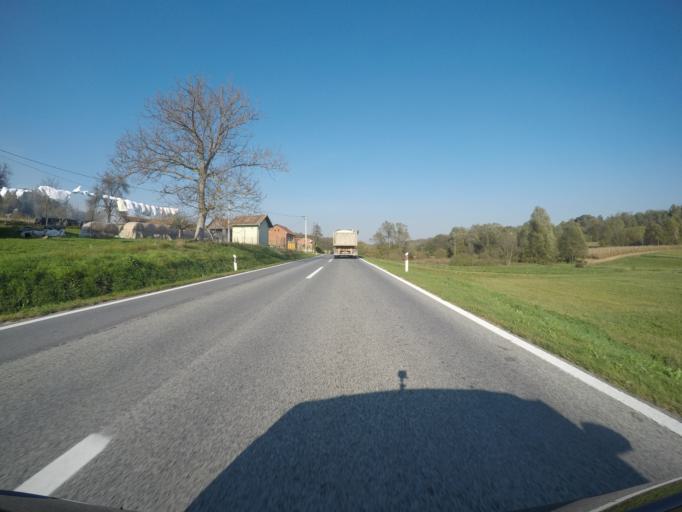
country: HR
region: Koprivnicko-Krizevacka
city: Virje
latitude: 45.9999
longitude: 16.9192
